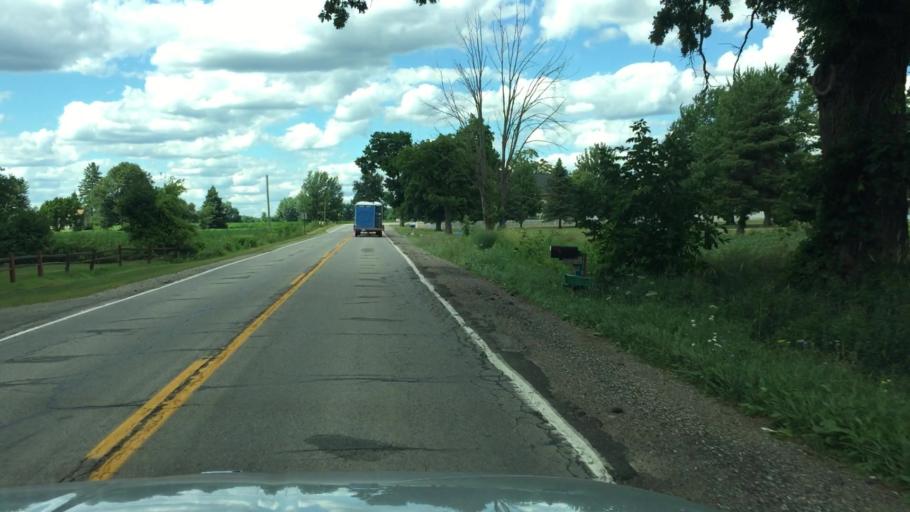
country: US
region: Michigan
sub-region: Saint Clair County
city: Capac
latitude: 42.9414
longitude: -82.9460
